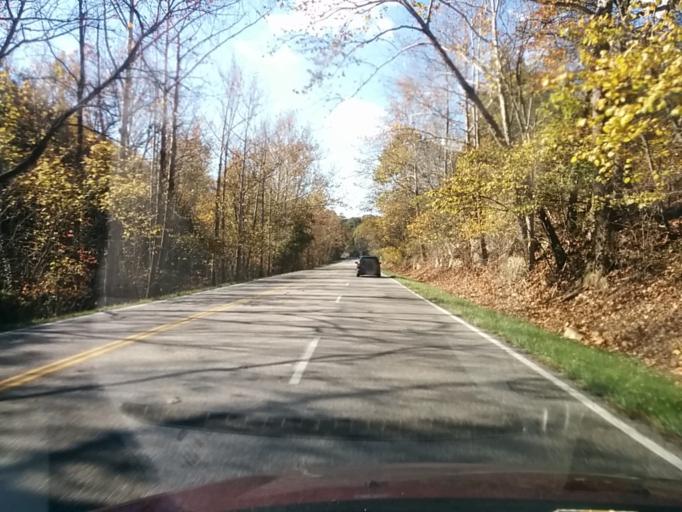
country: US
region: Virginia
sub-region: City of Lexington
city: Lexington
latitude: 37.7276
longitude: -79.4675
